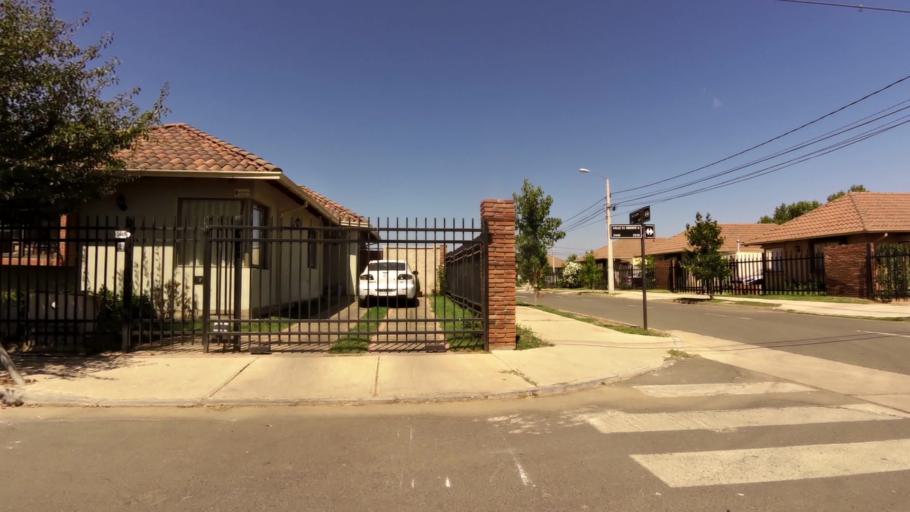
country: CL
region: Maule
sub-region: Provincia de Talca
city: Talca
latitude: -35.4331
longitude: -71.5965
